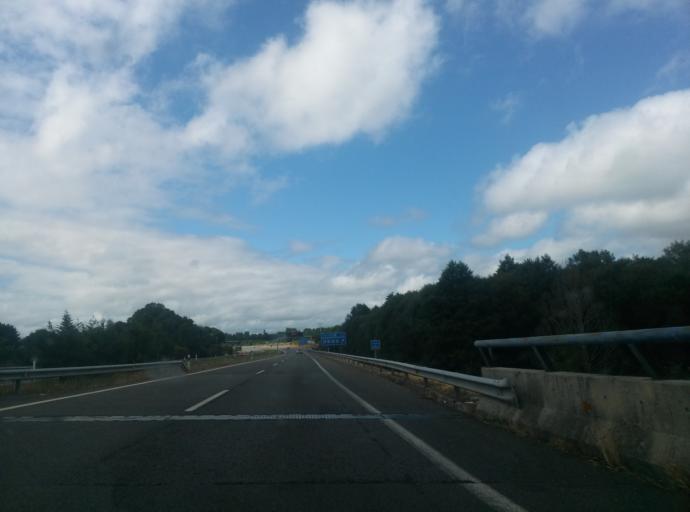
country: ES
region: Galicia
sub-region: Provincia de Lugo
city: Rabade
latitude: 43.1215
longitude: -7.6118
